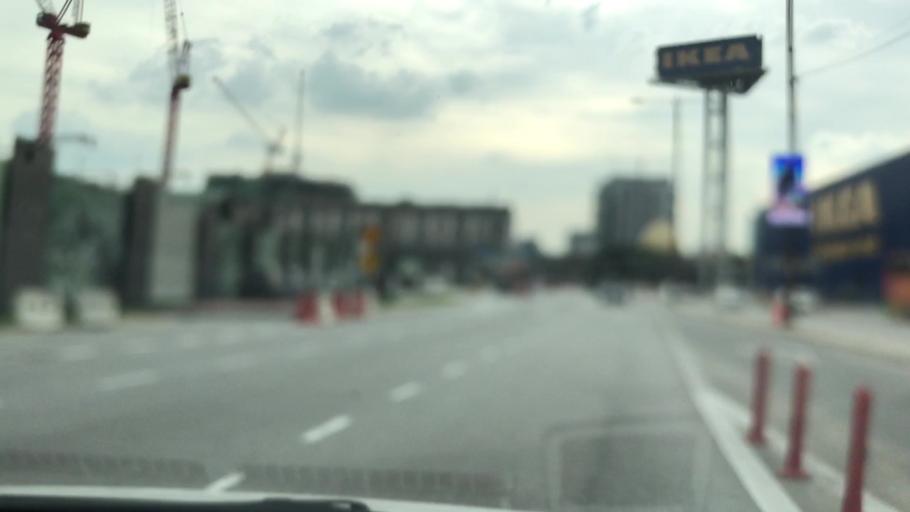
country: MY
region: Kuala Lumpur
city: Kuala Lumpur
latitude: 3.1338
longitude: 101.7217
